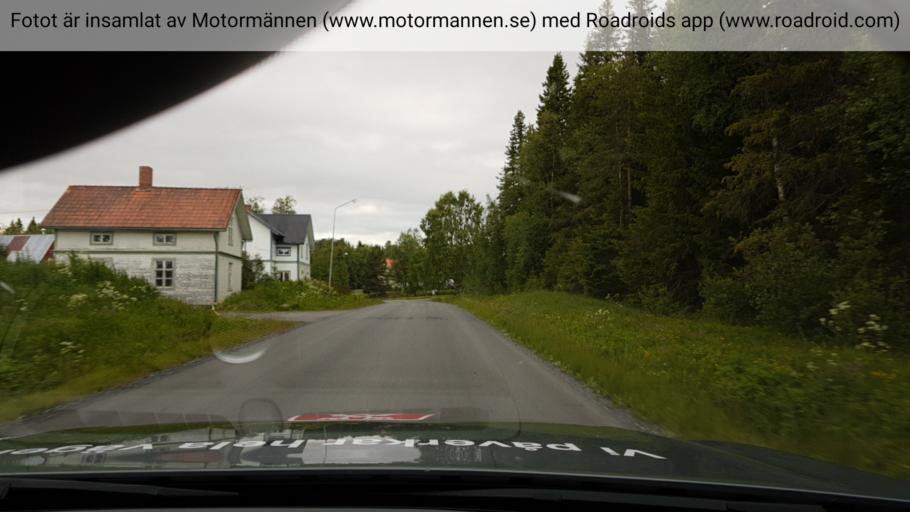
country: SE
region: Jaemtland
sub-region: OEstersunds Kommun
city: Lit
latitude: 63.5645
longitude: 14.9346
